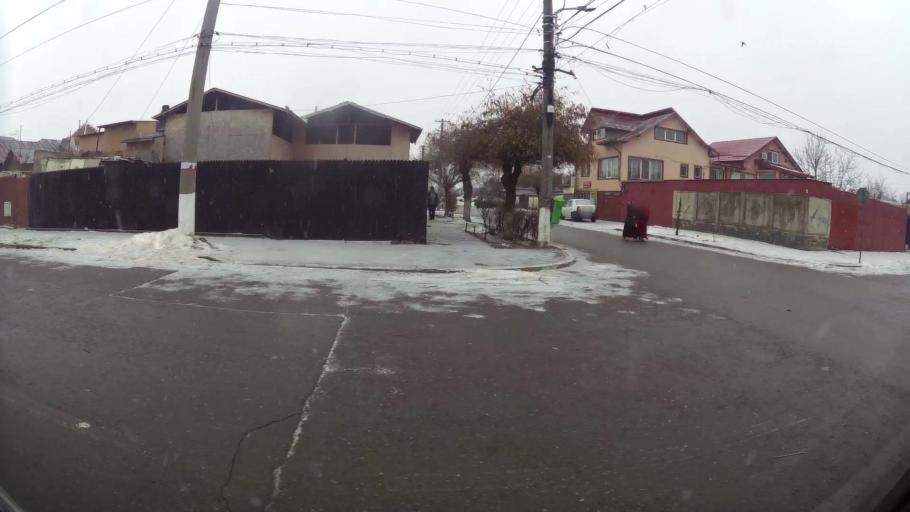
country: RO
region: Prahova
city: Ploiesti
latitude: 44.9486
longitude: 26.0496
